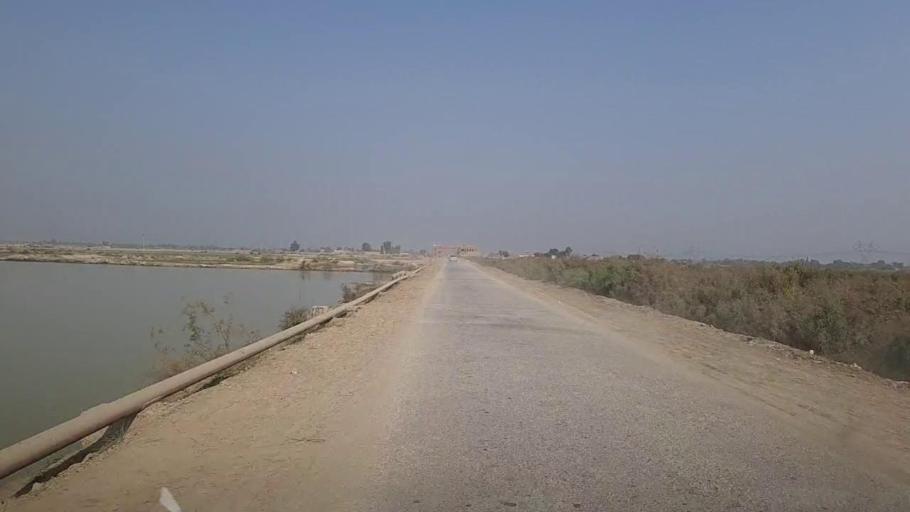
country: PK
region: Sindh
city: Kandhkot
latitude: 28.2266
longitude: 69.2050
